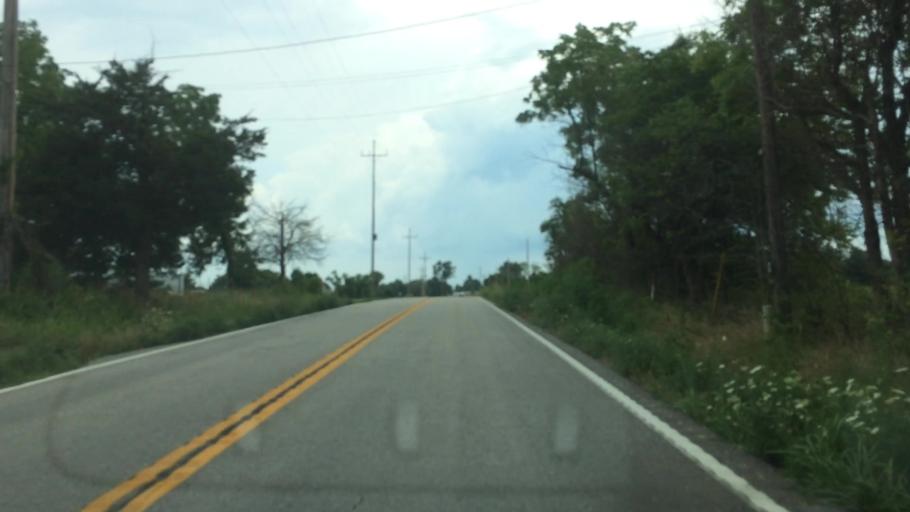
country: US
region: Missouri
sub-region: Greene County
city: Strafford
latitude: 37.2588
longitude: -93.1352
